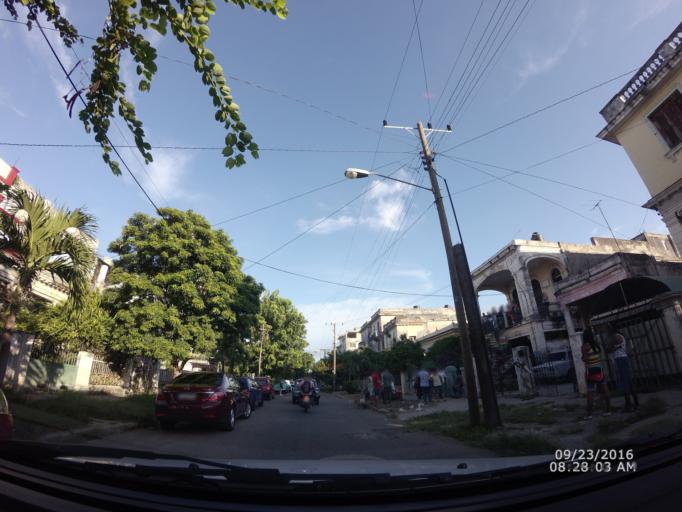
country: CU
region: La Habana
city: Havana
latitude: 23.1333
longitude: -82.3929
